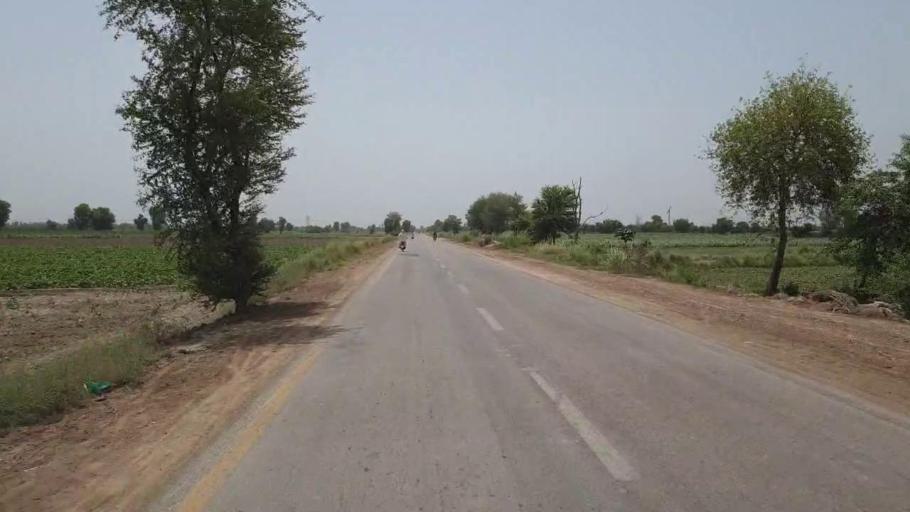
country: PK
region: Sindh
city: Moro
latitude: 26.6071
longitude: 68.0488
